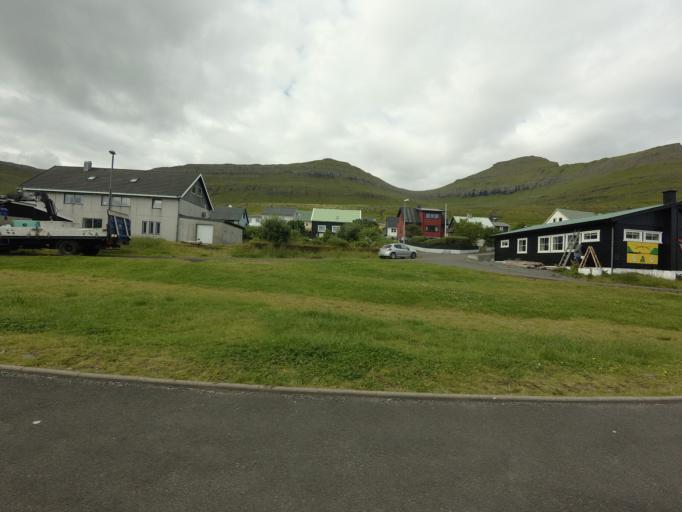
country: FO
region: Eysturoy
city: Eystur
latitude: 62.2121
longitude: -6.7105
